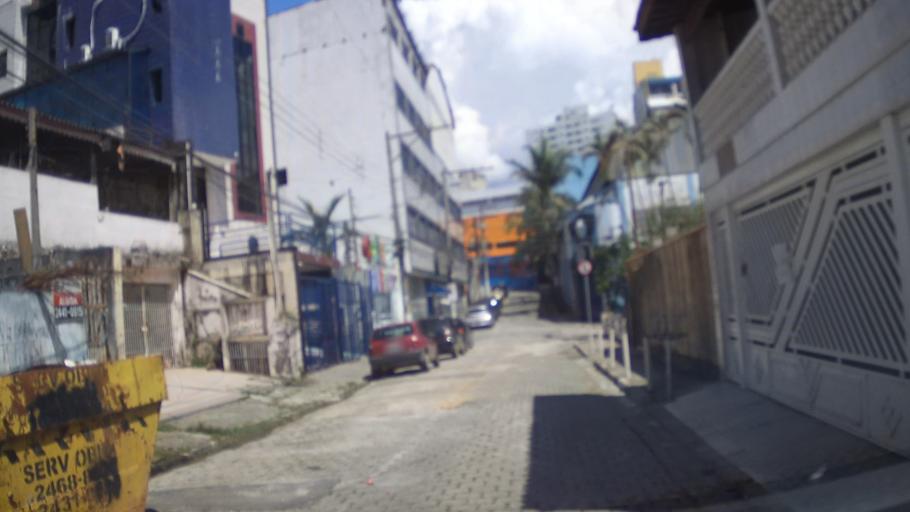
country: BR
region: Sao Paulo
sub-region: Guarulhos
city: Guarulhos
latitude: -23.4635
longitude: -46.5329
